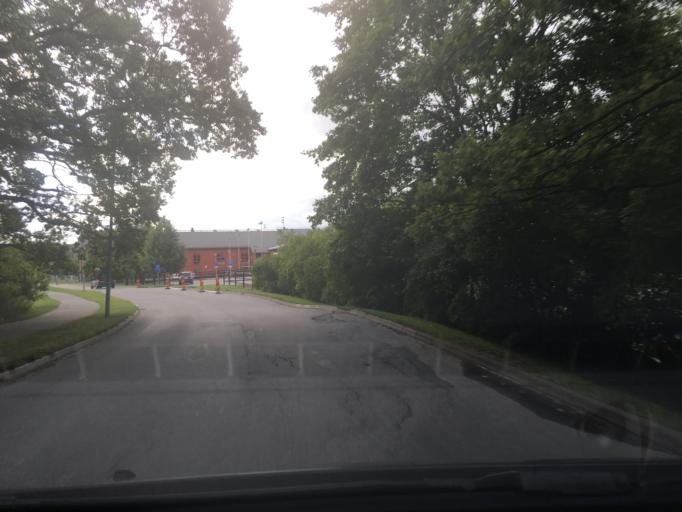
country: SE
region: Stockholm
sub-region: Stockholms Kommun
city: Bromma
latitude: 59.3398
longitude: 17.9262
